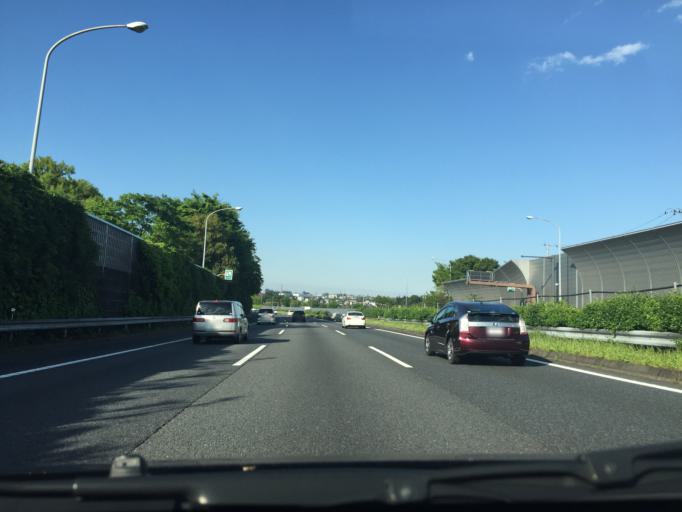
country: JP
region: Kanagawa
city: Minami-rinkan
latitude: 35.4867
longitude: 139.4668
